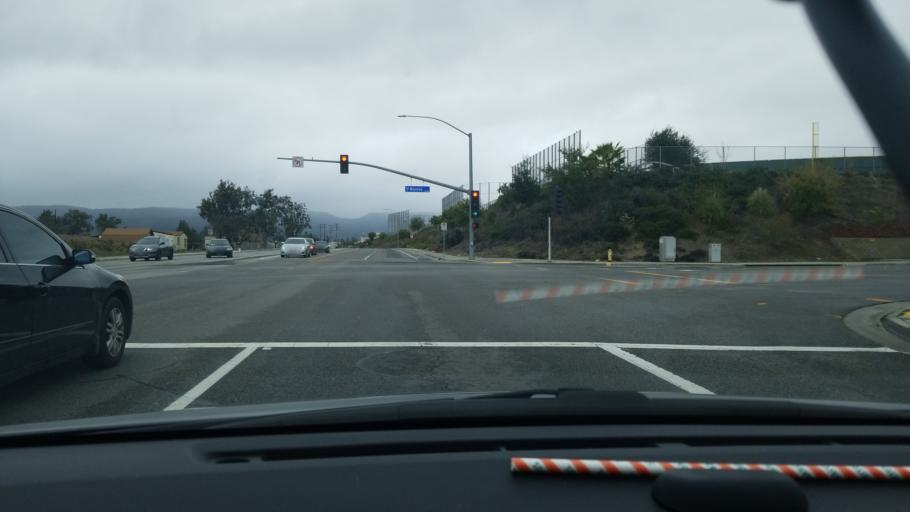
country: US
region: California
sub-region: Riverside County
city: Murrieta
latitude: 33.5627
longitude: -117.1950
